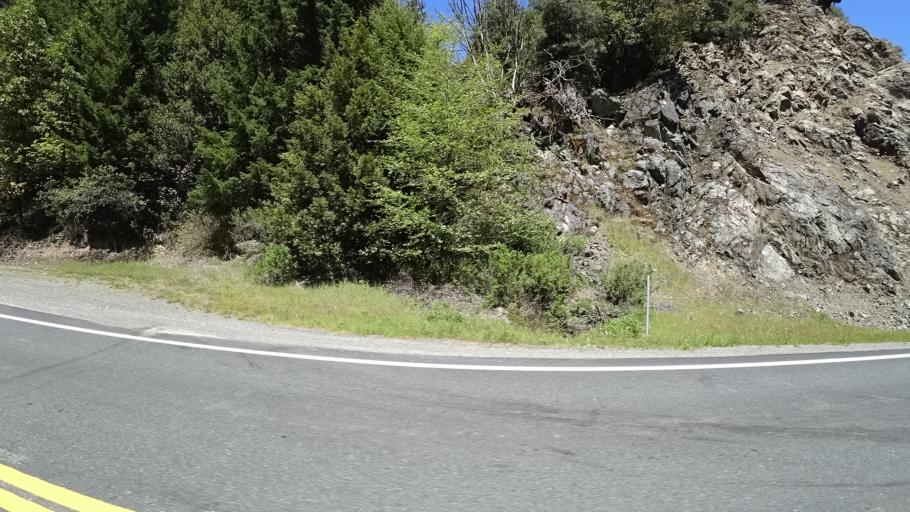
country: US
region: California
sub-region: Humboldt County
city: Willow Creek
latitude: 40.9249
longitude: -123.6906
